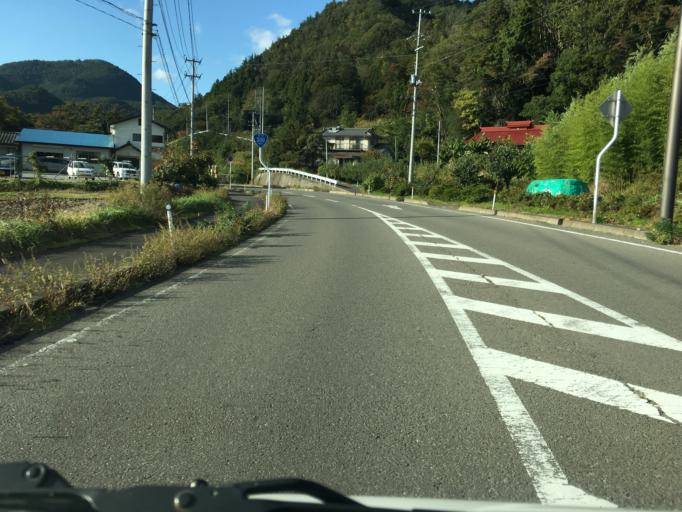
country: JP
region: Fukushima
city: Fukushima-shi
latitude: 37.8415
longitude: 140.4457
